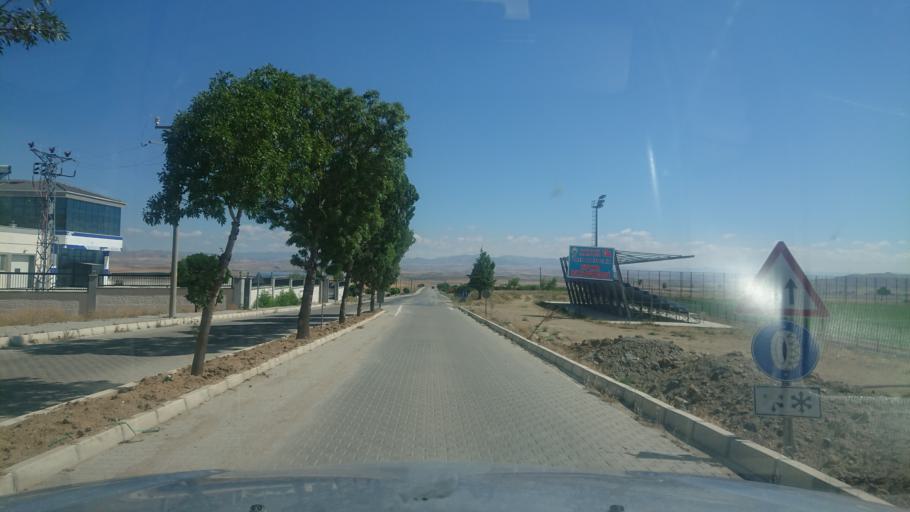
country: TR
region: Aksaray
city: Sariyahsi
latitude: 38.9915
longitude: 33.8475
